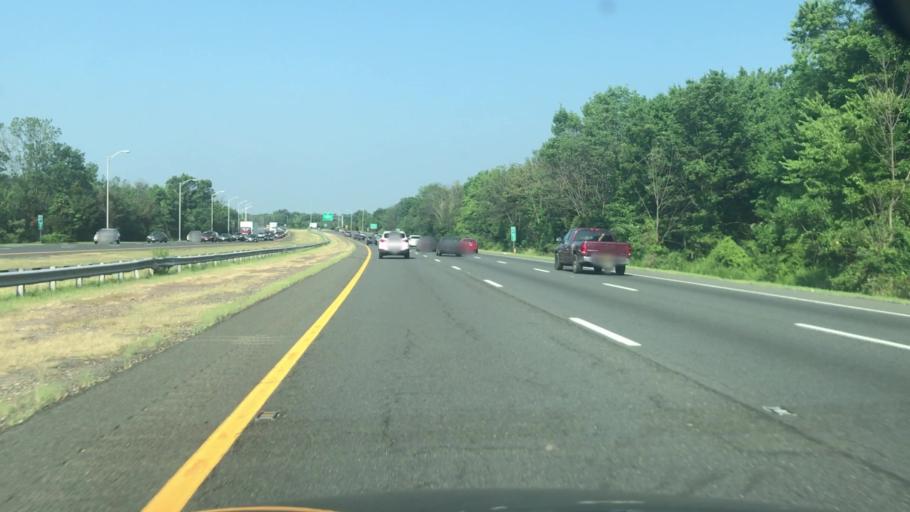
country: US
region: New Jersey
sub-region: Middlesex County
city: Middlesex
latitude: 40.5558
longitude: -74.4785
